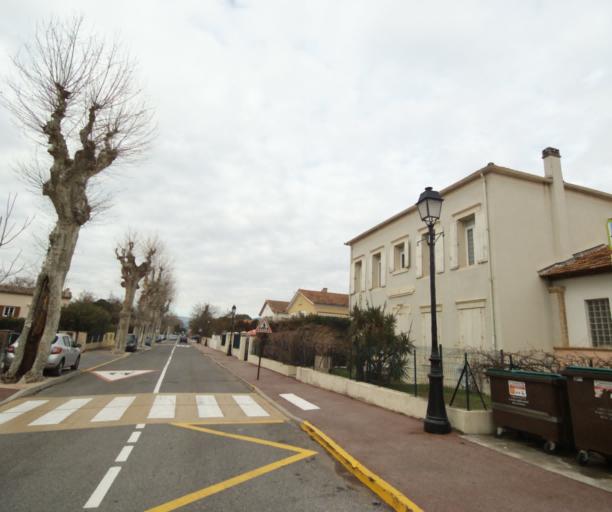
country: FR
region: Provence-Alpes-Cote d'Azur
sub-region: Departement du Var
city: Trans-en-Provence
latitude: 43.5052
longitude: 6.4843
